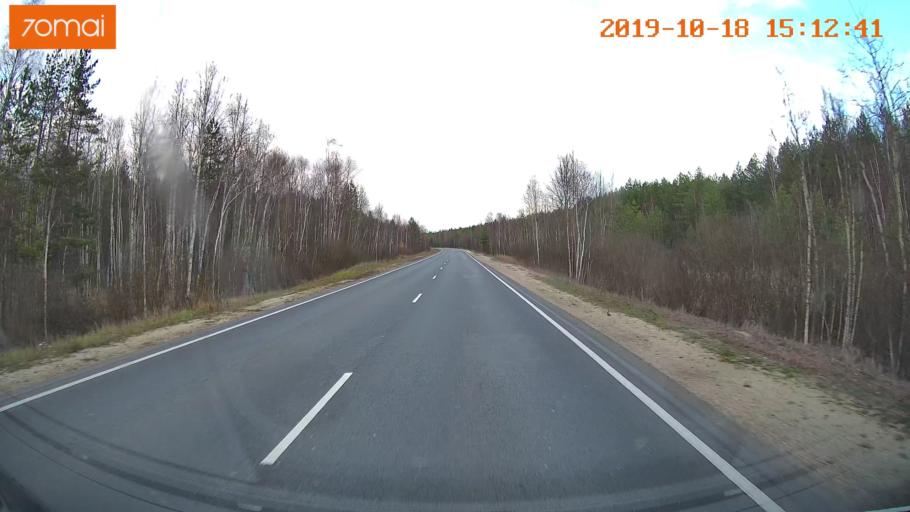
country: RU
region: Vladimir
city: Gus'-Khrustal'nyy
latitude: 55.5777
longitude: 40.7035
